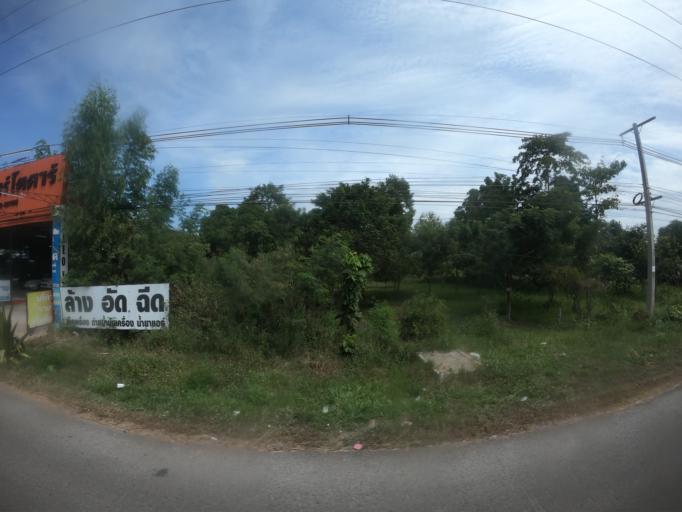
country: TH
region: Maha Sarakham
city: Chiang Yuen
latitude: 16.4186
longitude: 103.0786
